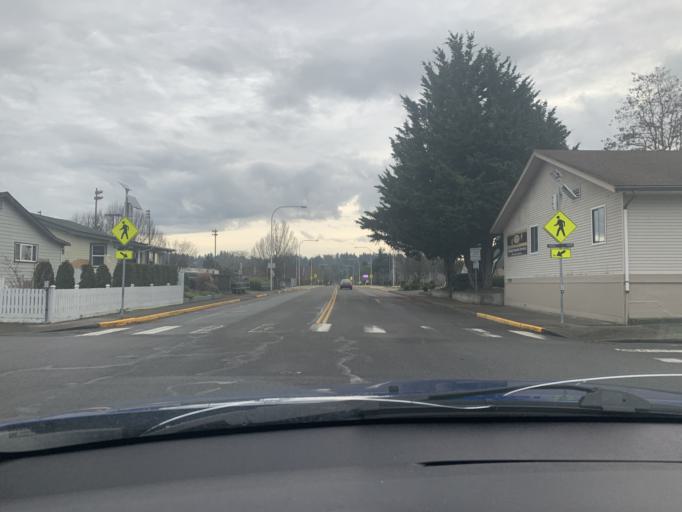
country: US
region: Washington
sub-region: King County
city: Auburn
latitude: 47.3108
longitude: -122.2231
